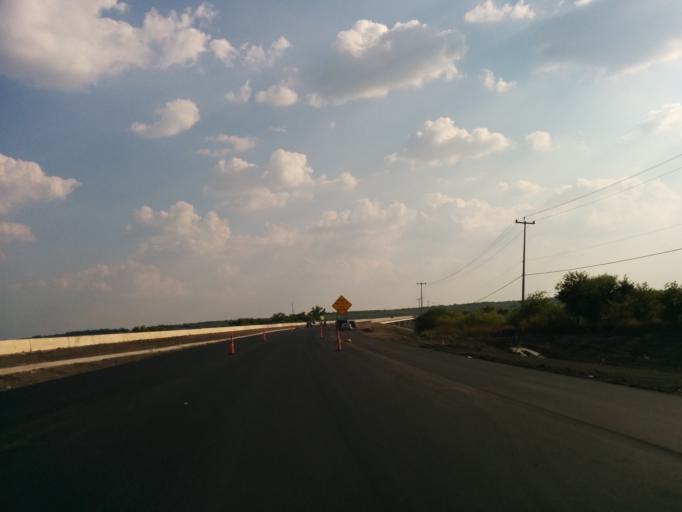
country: US
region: Texas
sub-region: Bexar County
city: Converse
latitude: 29.4883
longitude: -98.2915
